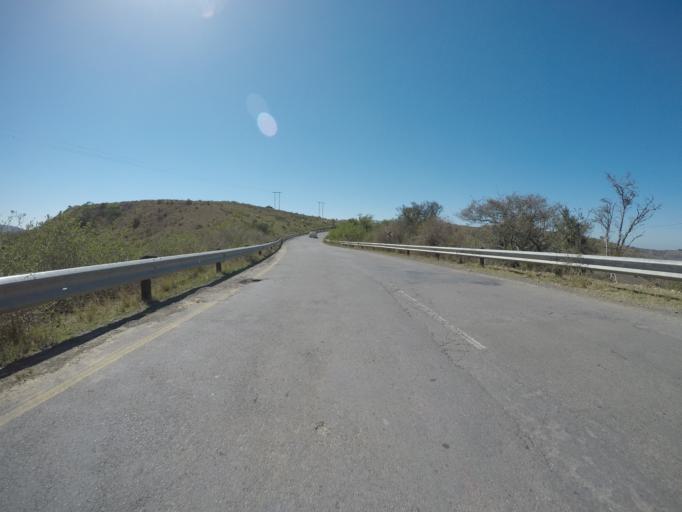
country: ZA
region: Eastern Cape
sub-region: OR Tambo District Municipality
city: Mthatha
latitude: -31.9095
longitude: 28.9533
